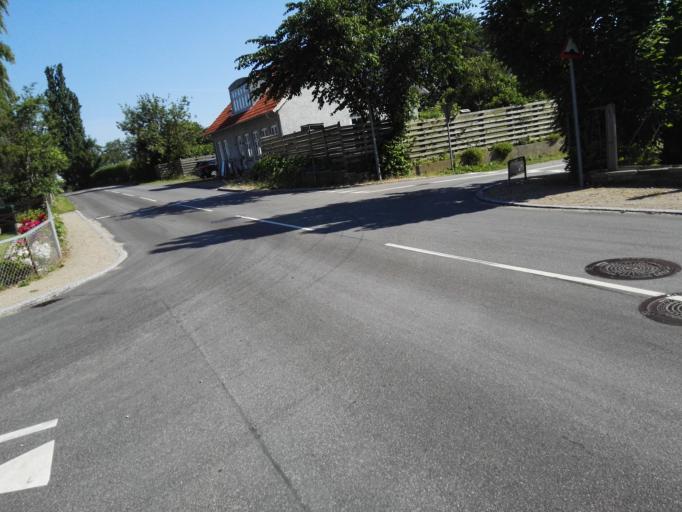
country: DK
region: Zealand
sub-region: Lejre Kommune
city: Ejby
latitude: 55.7185
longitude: 11.8904
